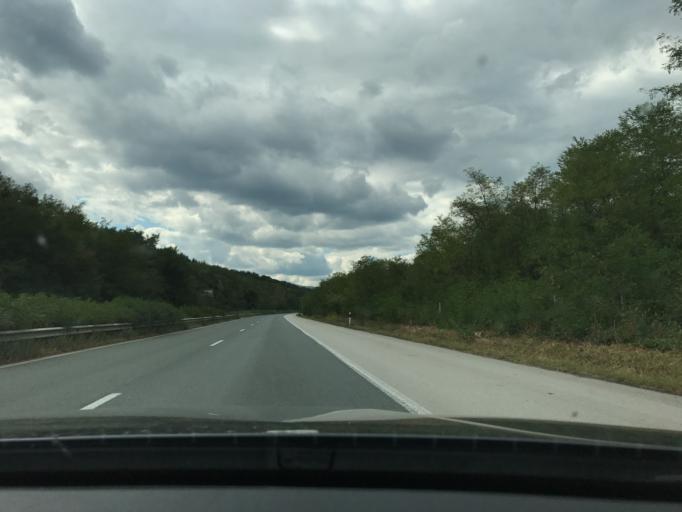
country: BG
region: Sofiya
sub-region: Obshtina Botevgrad
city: Botevgrad
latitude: 42.8951
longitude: 23.8408
